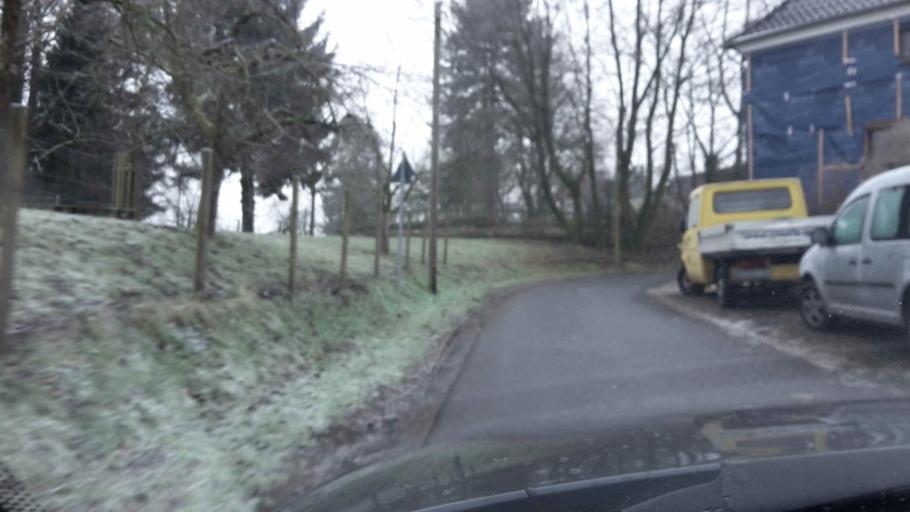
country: DE
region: North Rhine-Westphalia
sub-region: Regierungsbezirk Koln
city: Hennef
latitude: 50.7203
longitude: 7.3021
